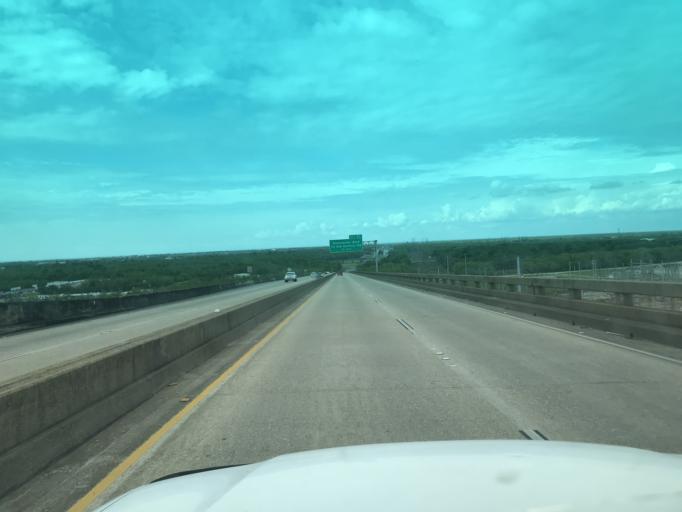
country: US
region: Louisiana
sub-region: Saint Bernard Parish
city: Chalmette
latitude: 30.0069
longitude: -89.9392
